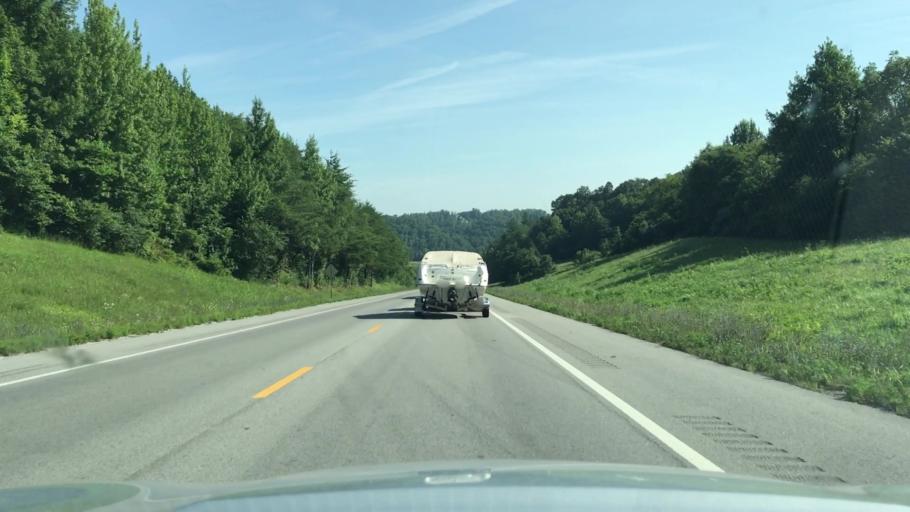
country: US
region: Tennessee
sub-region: Pickett County
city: Byrdstown
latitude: 36.5958
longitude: -85.1229
